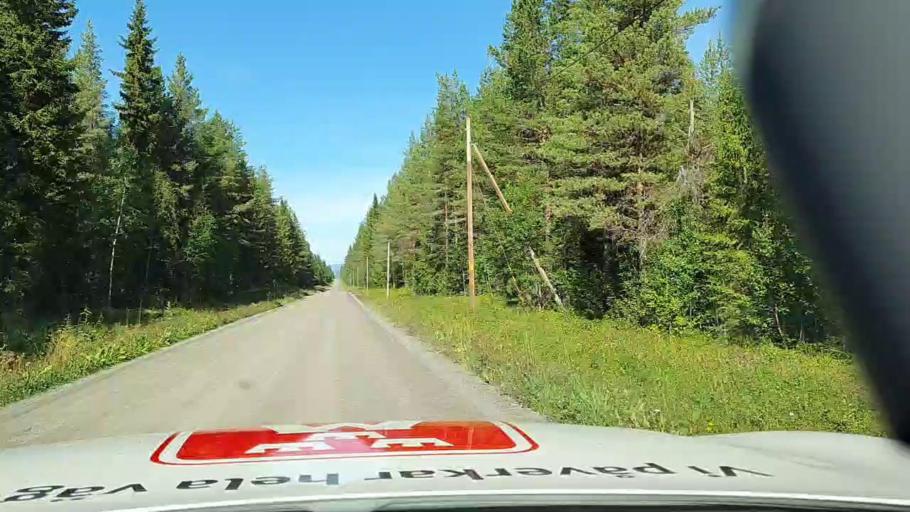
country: SE
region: Jaemtland
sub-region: Krokoms Kommun
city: Krokom
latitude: 63.6872
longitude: 14.6049
